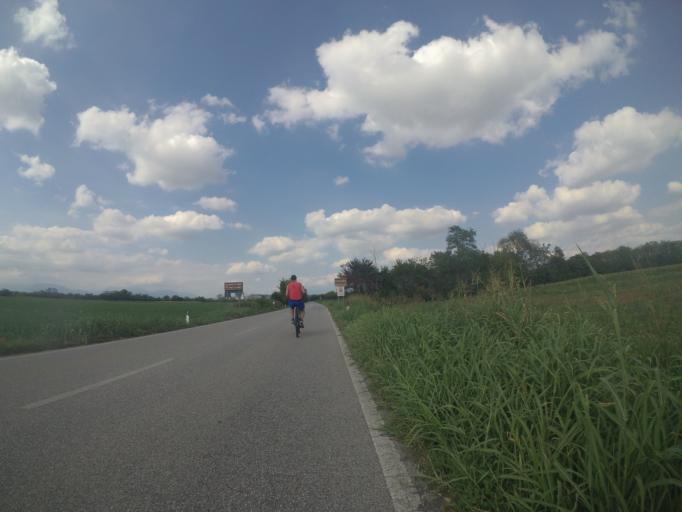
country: IT
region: Friuli Venezia Giulia
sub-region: Provincia di Udine
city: San Vito di Fagagna
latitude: 46.0750
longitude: 13.0847
